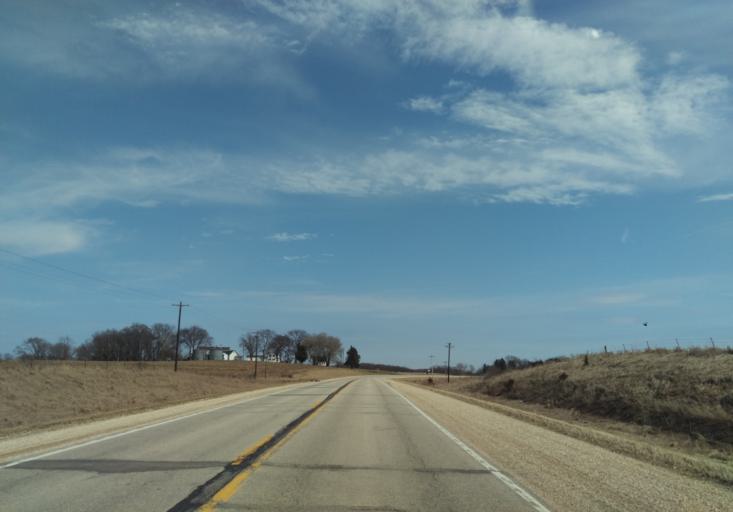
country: US
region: Wisconsin
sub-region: Crawford County
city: Prairie du Chien
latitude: 43.1391
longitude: -91.2429
